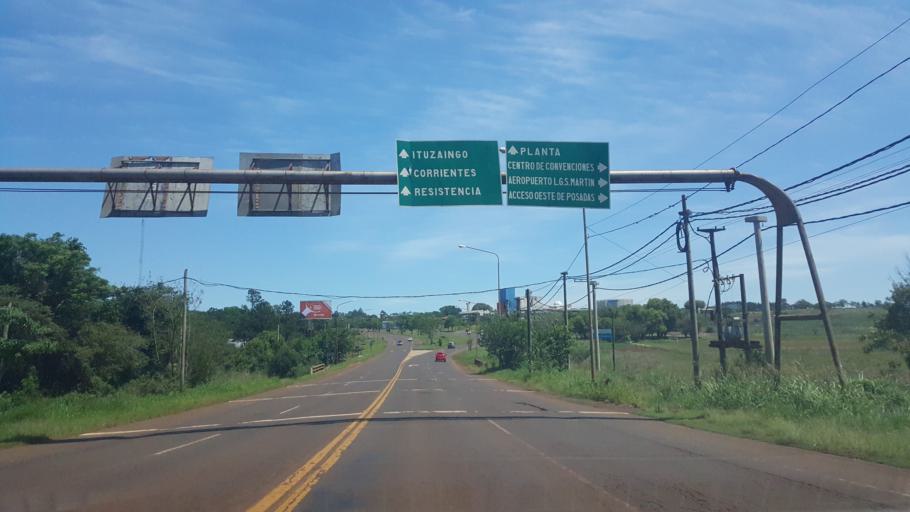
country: AR
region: Misiones
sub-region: Departamento de Capital
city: Posadas
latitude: -27.3986
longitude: -55.9552
